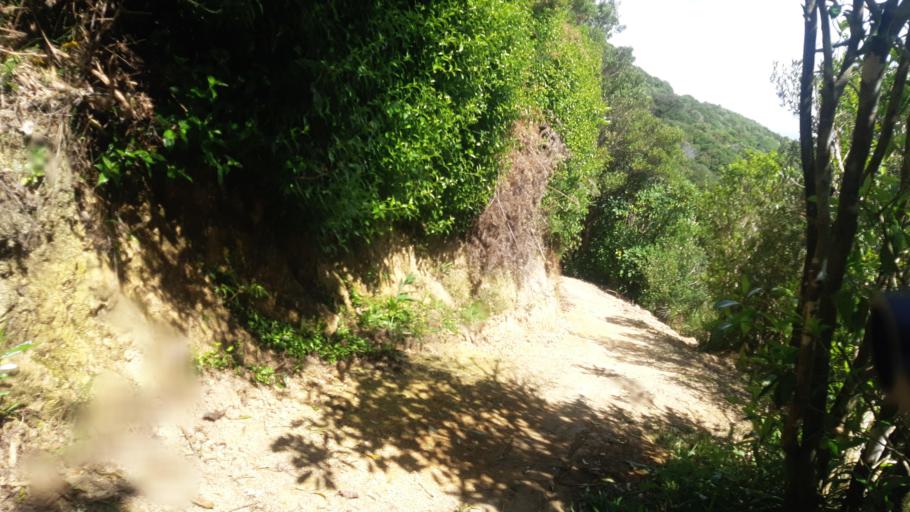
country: NZ
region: Marlborough
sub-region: Marlborough District
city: Picton
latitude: -41.2645
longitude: 174.0279
